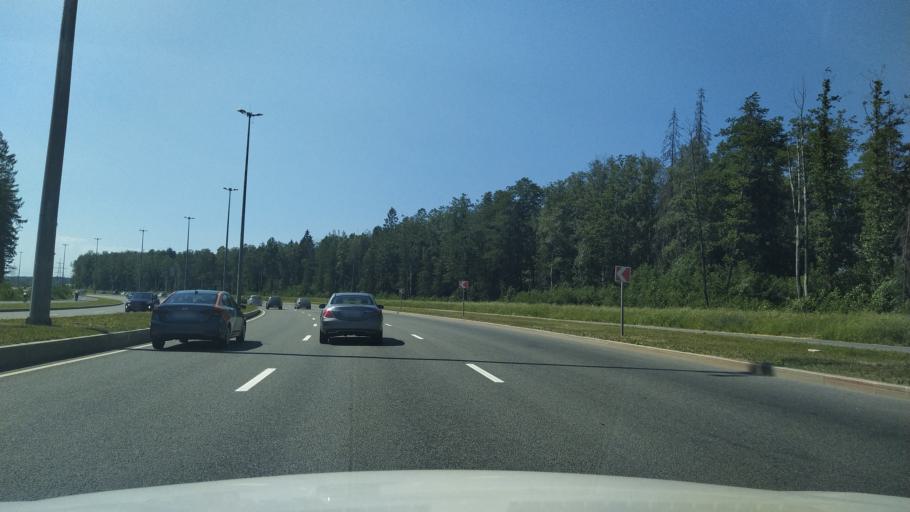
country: RU
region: St.-Petersburg
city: Levashovo
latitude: 60.0644
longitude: 30.2058
